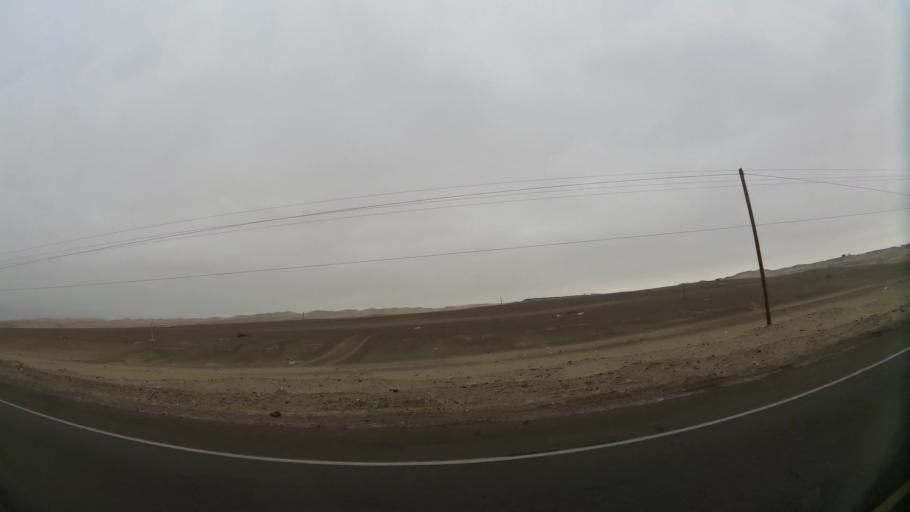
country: PE
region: Ica
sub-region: Provincia de Pisco
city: Paracas
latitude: -13.8927
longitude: -76.0911
